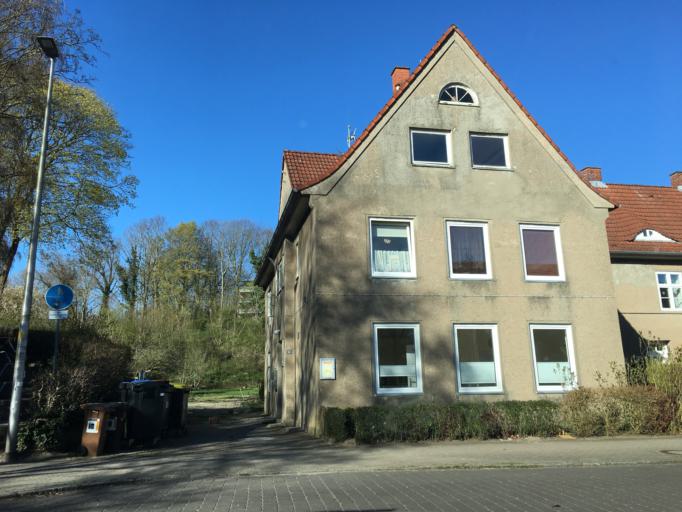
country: DE
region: Schleswig-Holstein
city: Eckernforde
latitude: 54.4755
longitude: 9.8289
